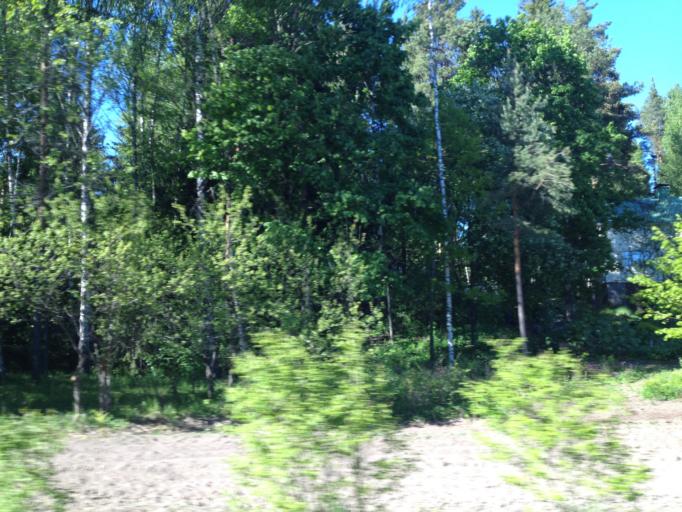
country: FI
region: Uusimaa
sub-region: Helsinki
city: Espoo
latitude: 60.2443
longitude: 24.5748
